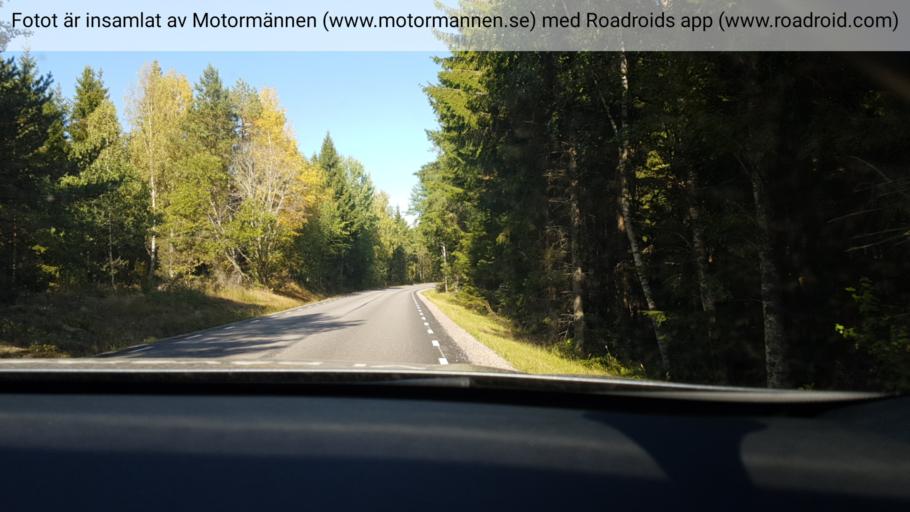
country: SE
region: Vaestra Goetaland
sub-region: Gotene Kommun
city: Goetene
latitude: 58.6325
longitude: 13.5243
